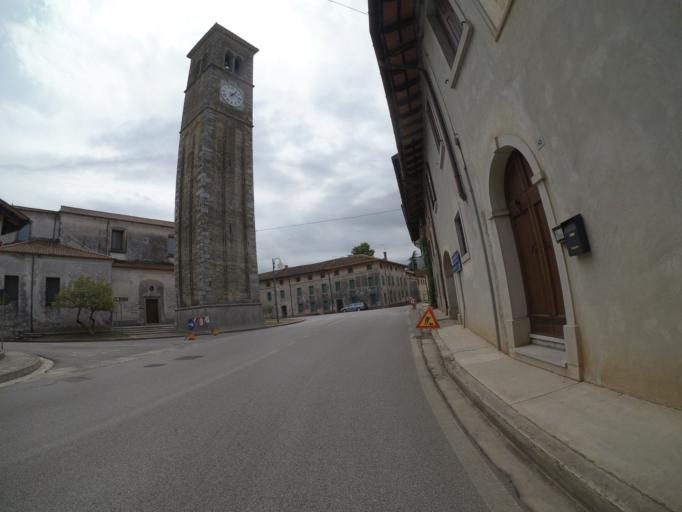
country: IT
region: Friuli Venezia Giulia
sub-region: Provincia di Udine
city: Sedegliano
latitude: 45.9999
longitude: 12.9977
